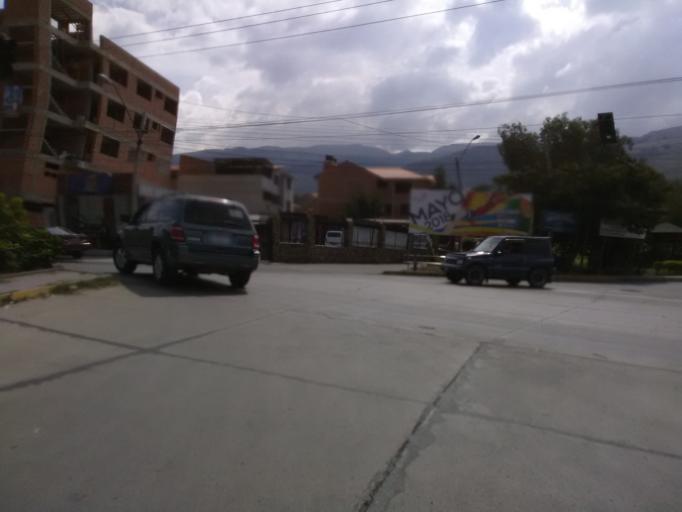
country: BO
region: Cochabamba
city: Cochabamba
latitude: -17.3673
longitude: -66.1490
